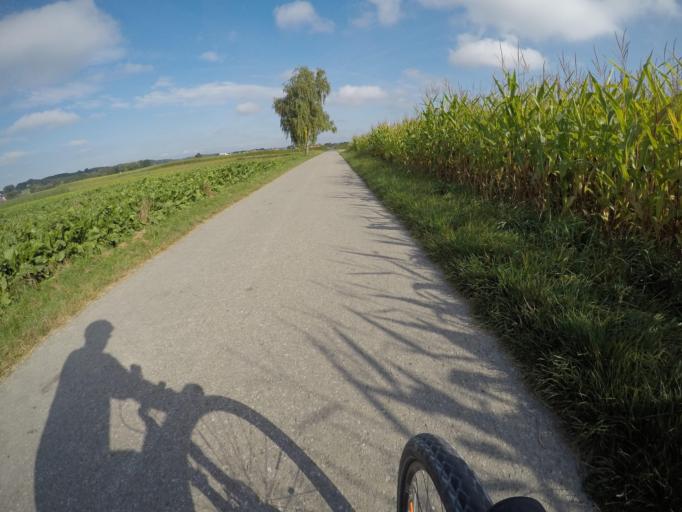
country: DE
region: Bavaria
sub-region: Swabia
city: Nordendorf
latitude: 48.5819
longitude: 10.8362
